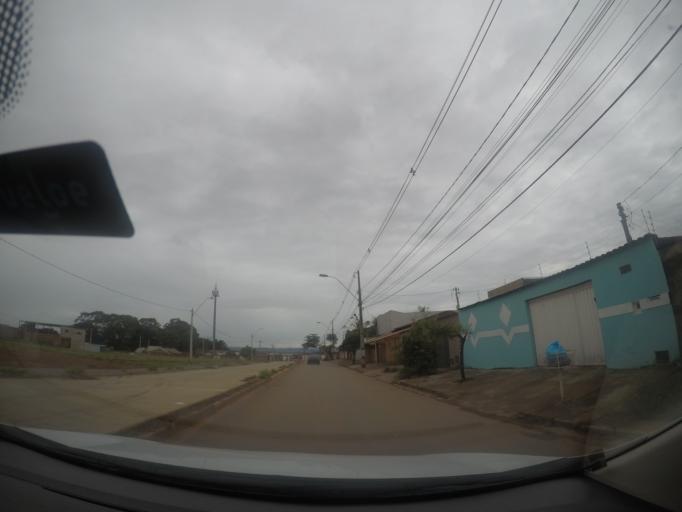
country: BR
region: Goias
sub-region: Goiania
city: Goiania
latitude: -16.6206
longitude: -49.3052
